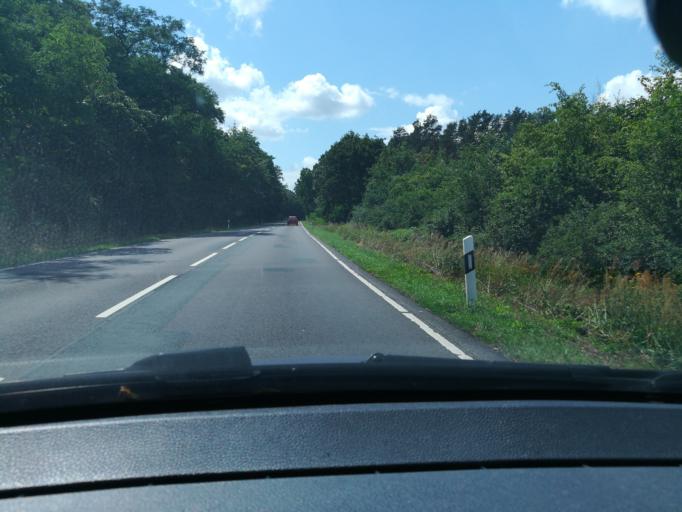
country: DE
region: Saxony-Anhalt
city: Zielitz
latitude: 52.2824
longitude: 11.6675
